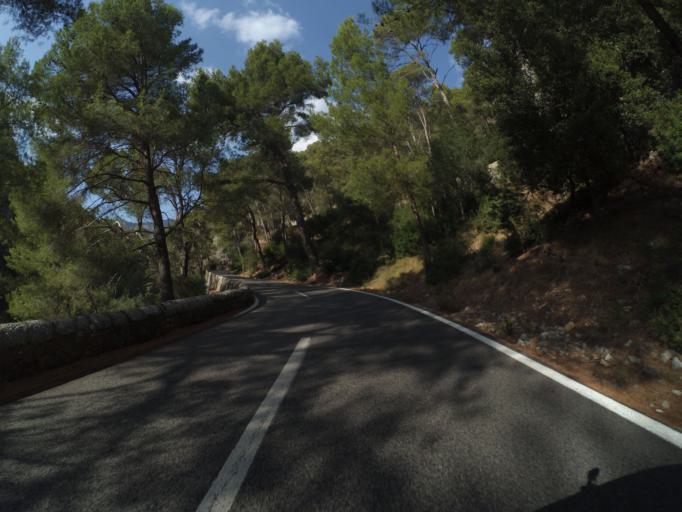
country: ES
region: Balearic Islands
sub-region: Illes Balears
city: Selva
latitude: 39.7771
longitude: 2.8982
